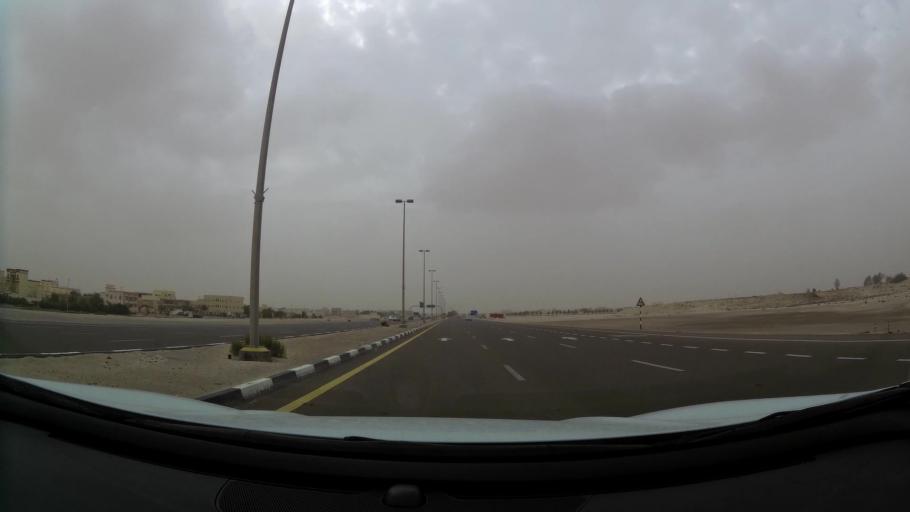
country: AE
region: Abu Dhabi
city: Abu Dhabi
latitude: 24.4056
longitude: 54.7162
